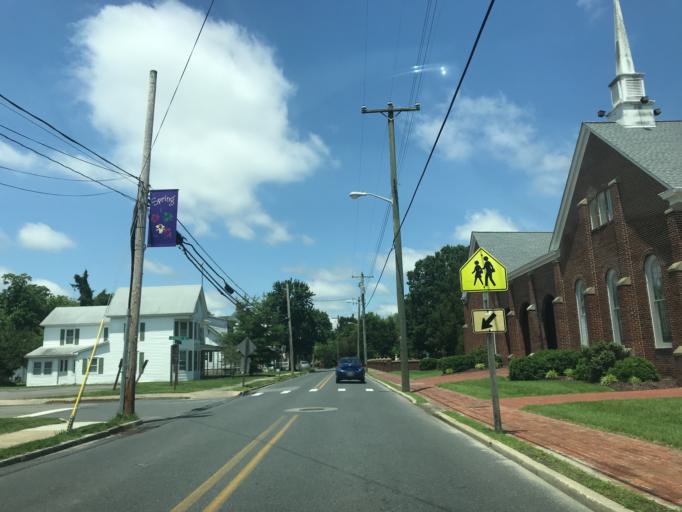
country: US
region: Maryland
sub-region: Caroline County
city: Federalsburg
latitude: 38.6962
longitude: -75.7745
